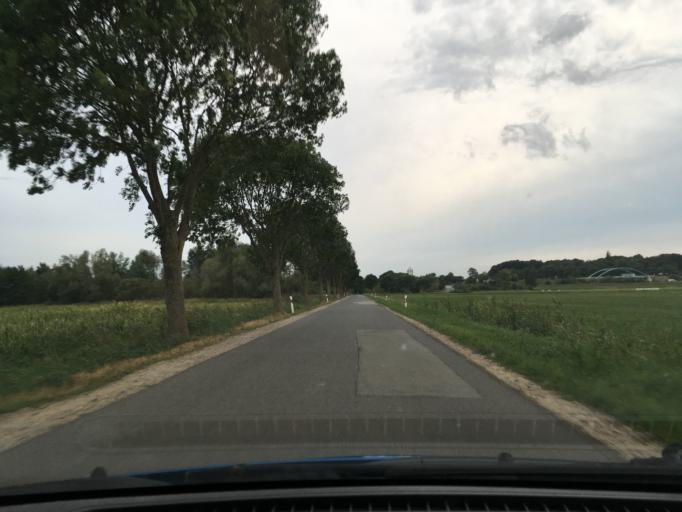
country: DE
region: Schleswig-Holstein
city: Lanze
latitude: 53.3782
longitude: 10.5944
